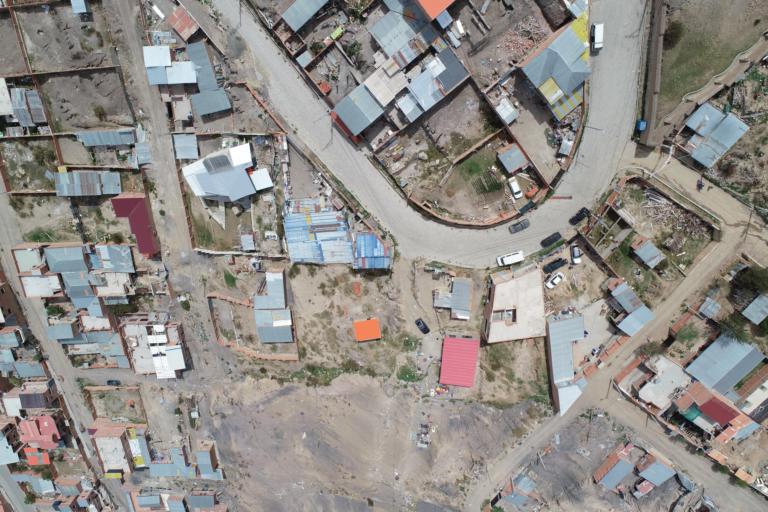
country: BO
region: La Paz
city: La Paz
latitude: -16.5529
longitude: -68.0520
